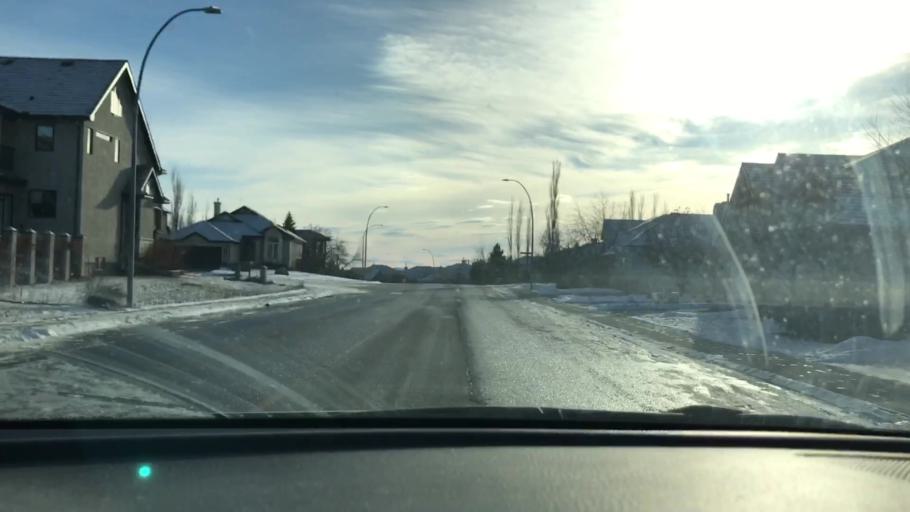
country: CA
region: Alberta
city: Calgary
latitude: 51.0244
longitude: -114.1772
